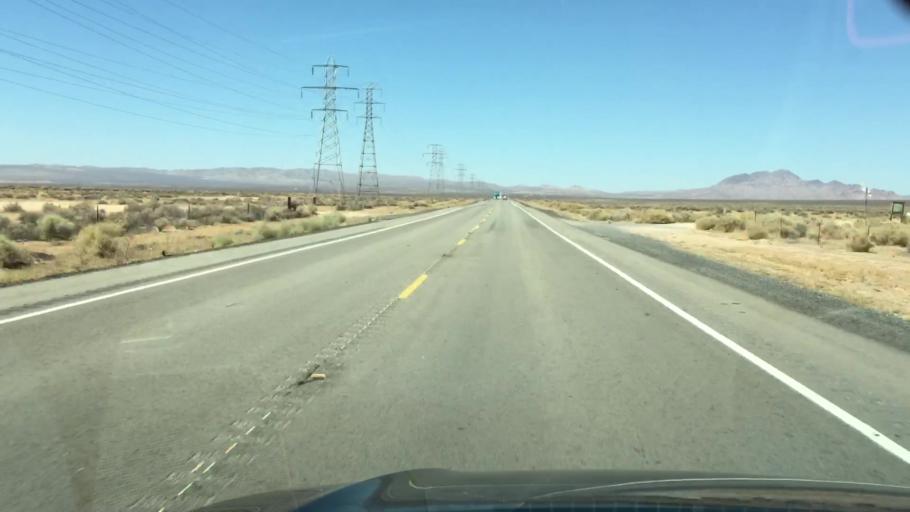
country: US
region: California
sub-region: Kern County
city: Boron
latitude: 35.1842
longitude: -117.5951
